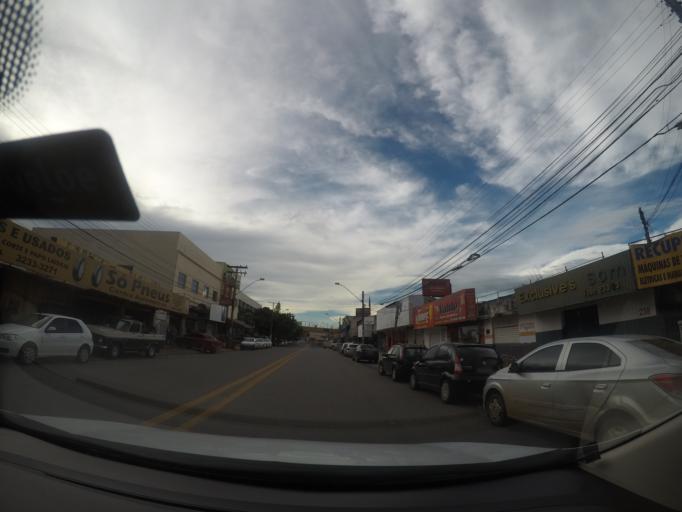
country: BR
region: Goias
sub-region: Goiania
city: Goiania
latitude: -16.6732
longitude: -49.2815
